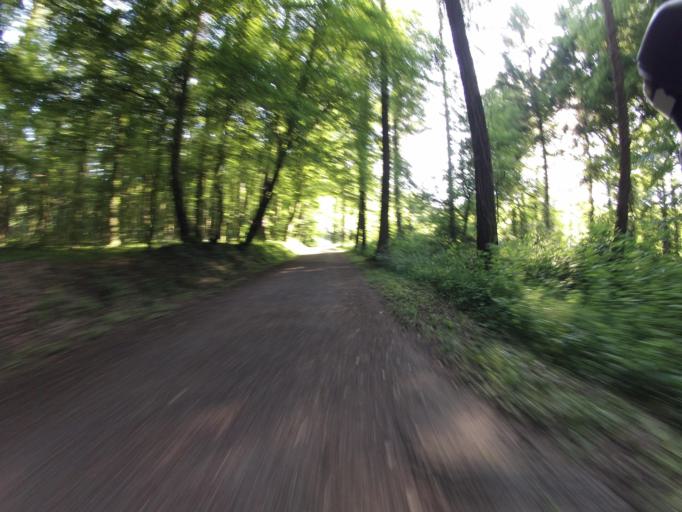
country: DE
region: Lower Saxony
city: Quendorf
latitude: 52.3173
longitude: 7.1970
